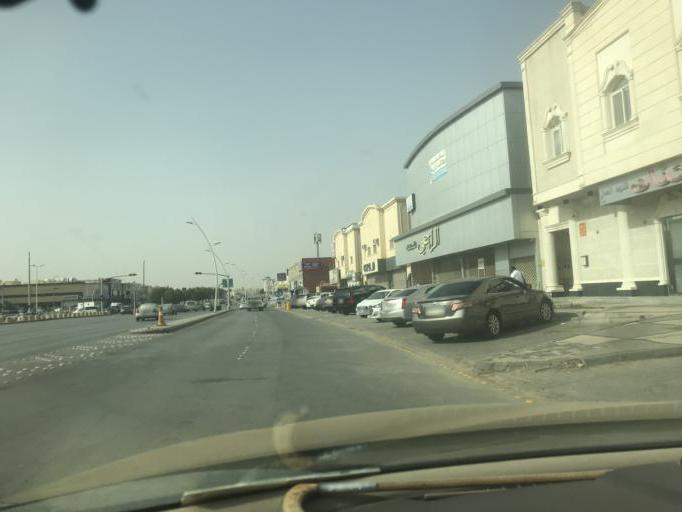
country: SA
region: Ar Riyad
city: Riyadh
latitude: 24.6819
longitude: 46.7986
